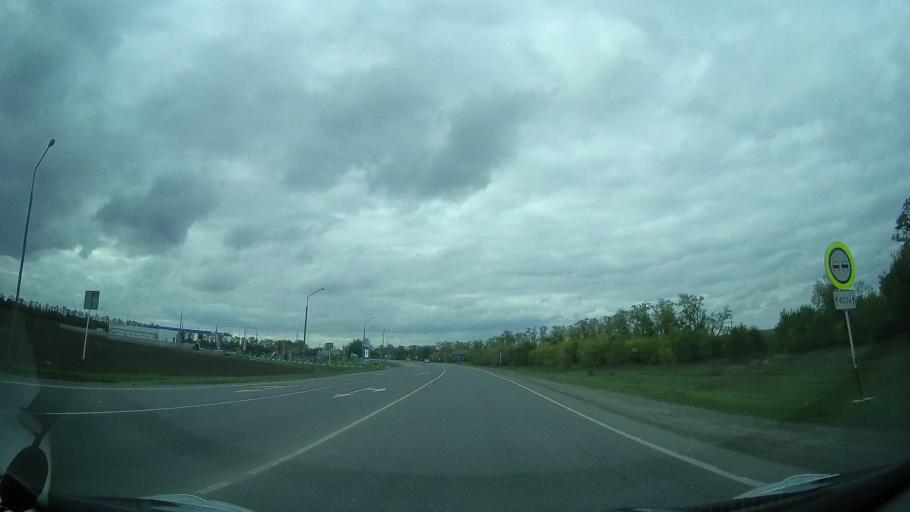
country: RU
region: Rostov
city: Mechetinskaya
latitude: 46.7550
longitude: 40.4569
